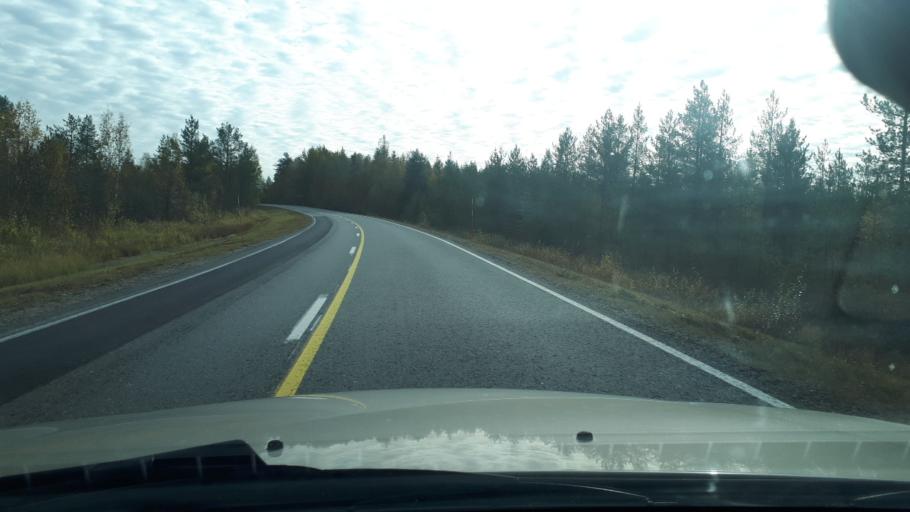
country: FI
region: Lapland
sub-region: Rovaniemi
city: Ranua
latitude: 65.9632
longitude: 26.0275
